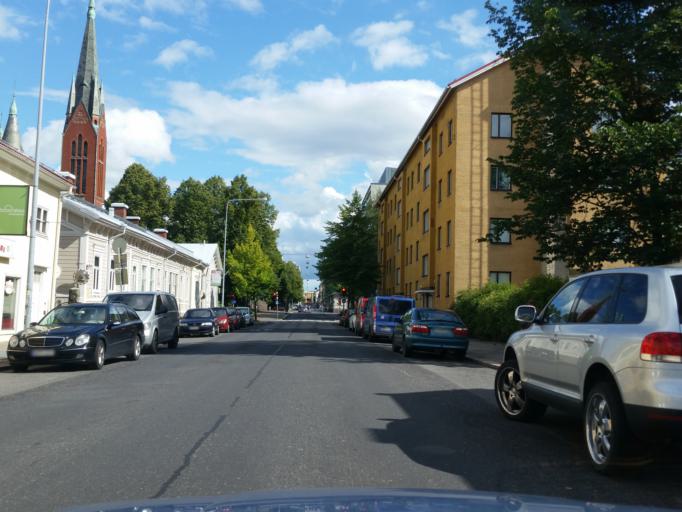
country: FI
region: Varsinais-Suomi
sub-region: Turku
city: Turku
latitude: 60.4475
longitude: 22.2463
